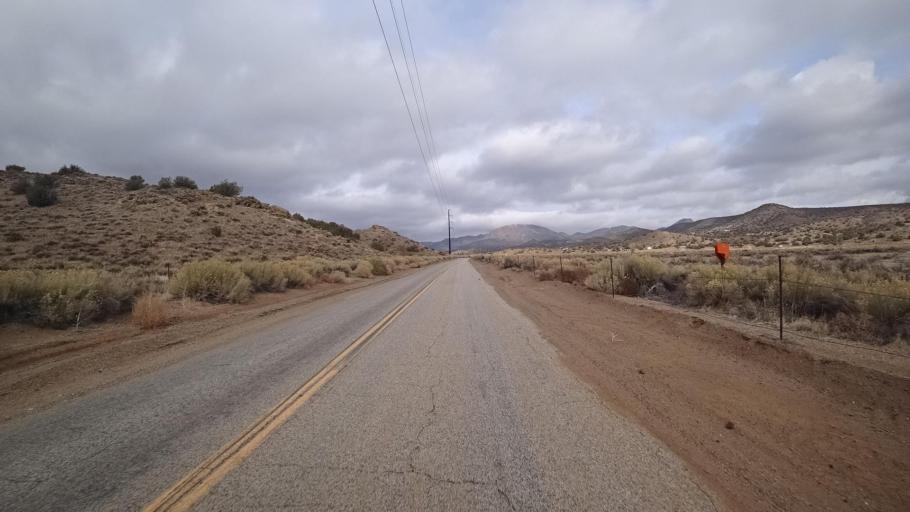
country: US
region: California
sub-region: Kern County
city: Tehachapi
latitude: 35.1566
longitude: -118.3219
